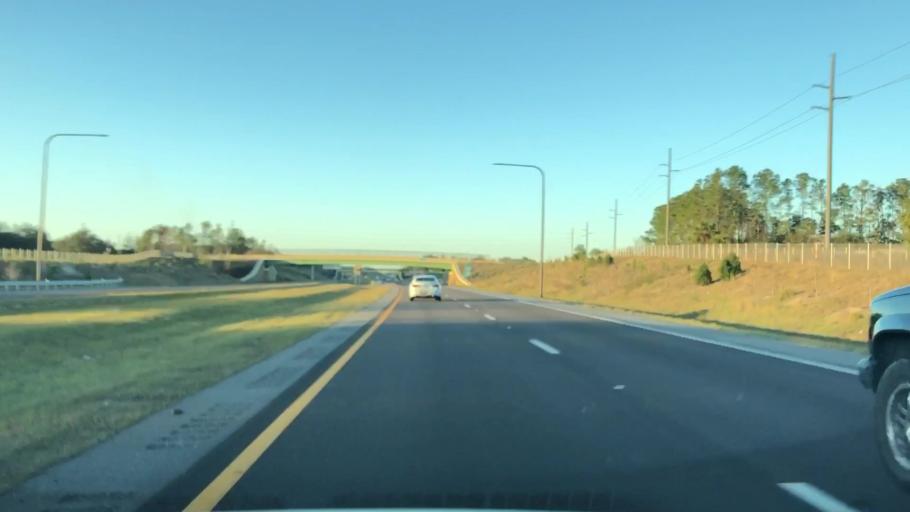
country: US
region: Florida
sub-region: Orange County
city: Zellwood
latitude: 28.7060
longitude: -81.5595
